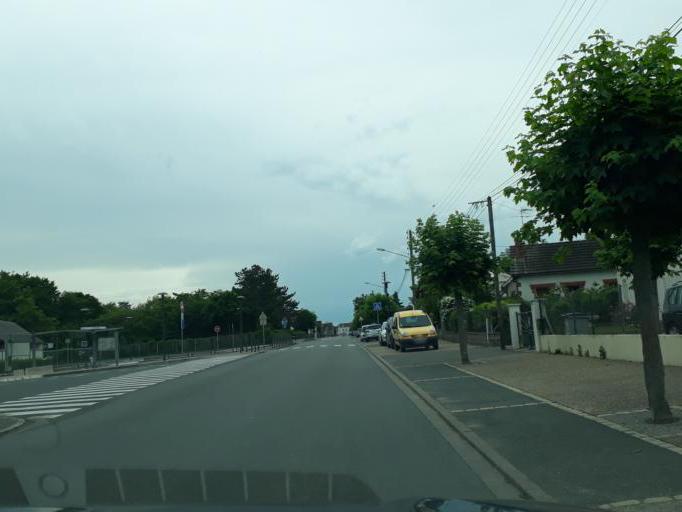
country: FR
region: Centre
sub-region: Departement du Loiret
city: Sully-sur-Loire
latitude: 47.7636
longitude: 2.3861
